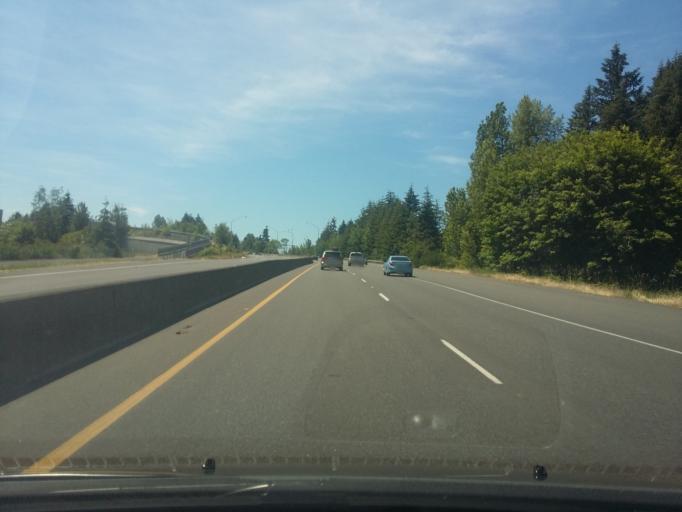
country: US
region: Washington
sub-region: Clark County
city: Five Corners
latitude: 45.6837
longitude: -122.5880
